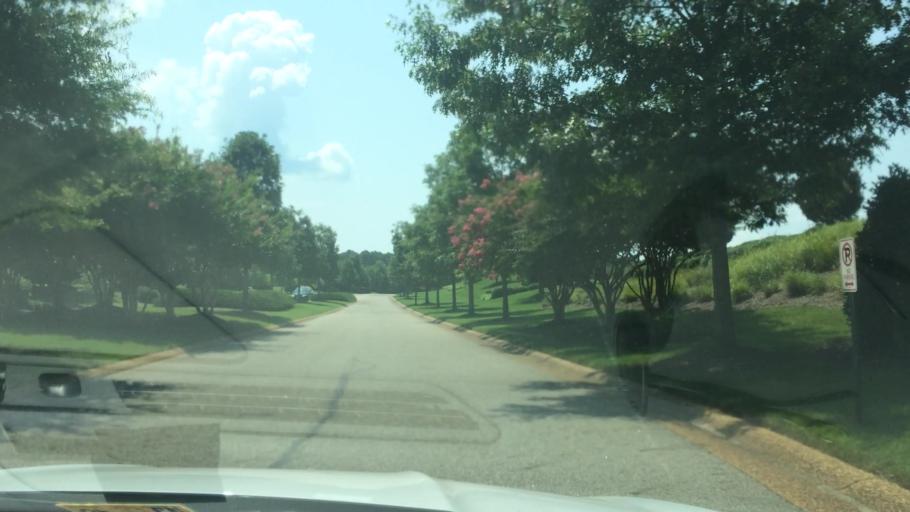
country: US
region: Virginia
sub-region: James City County
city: Williamsburg
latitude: 37.3502
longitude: -76.7671
